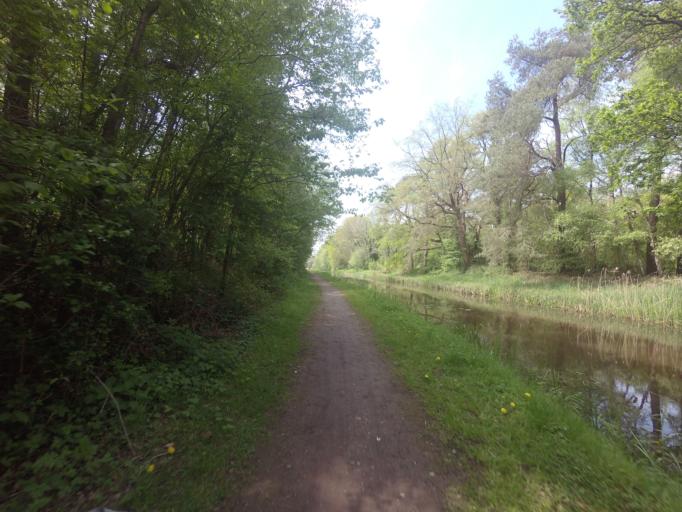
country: NL
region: Overijssel
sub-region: Gemeente Hof van Twente
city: Delden
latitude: 52.2171
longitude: 6.7140
